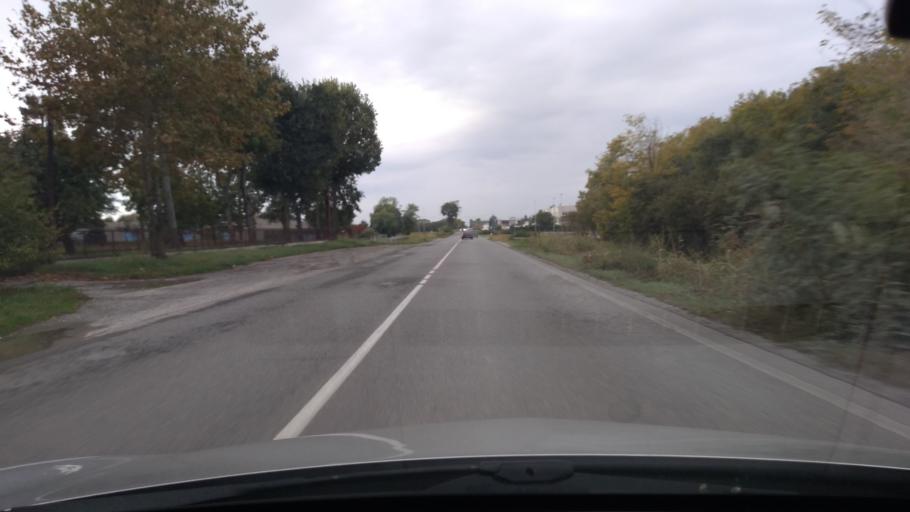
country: IT
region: Lombardy
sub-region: Provincia di Bergamo
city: Urgnano
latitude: 45.5912
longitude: 9.6928
